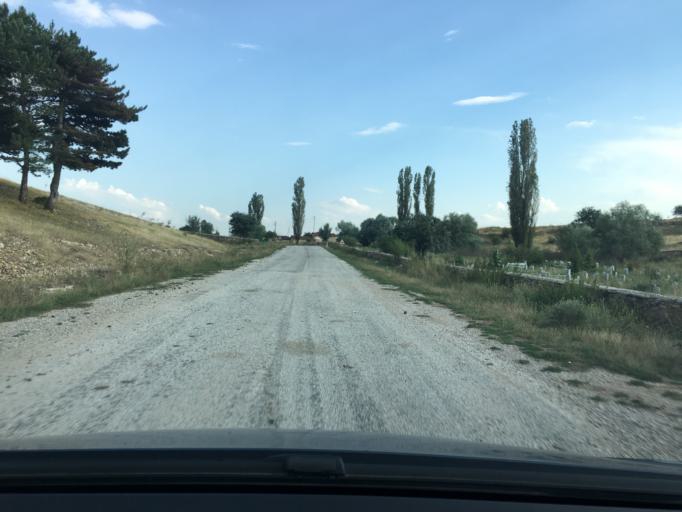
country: TR
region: Eskisehir
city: Kirka
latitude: 39.2811
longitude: 30.6740
